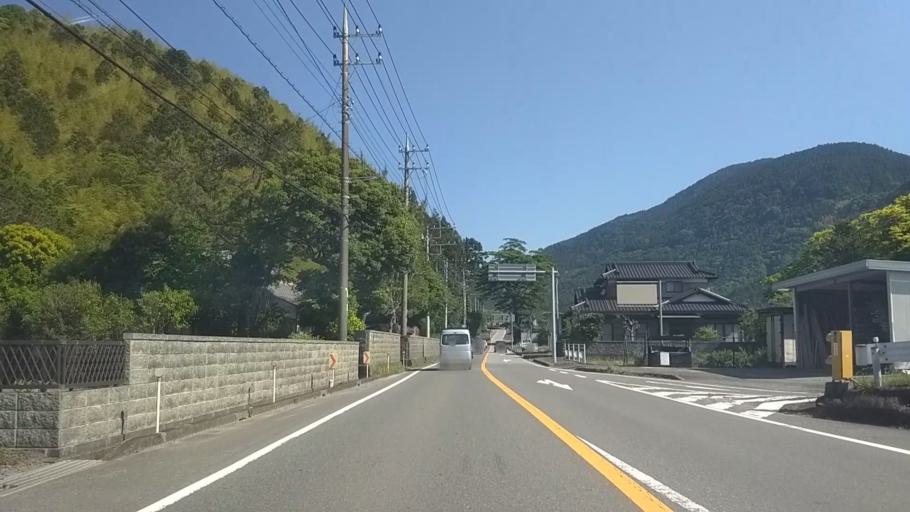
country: JP
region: Shizuoka
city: Fujinomiya
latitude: 35.2523
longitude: 138.4788
